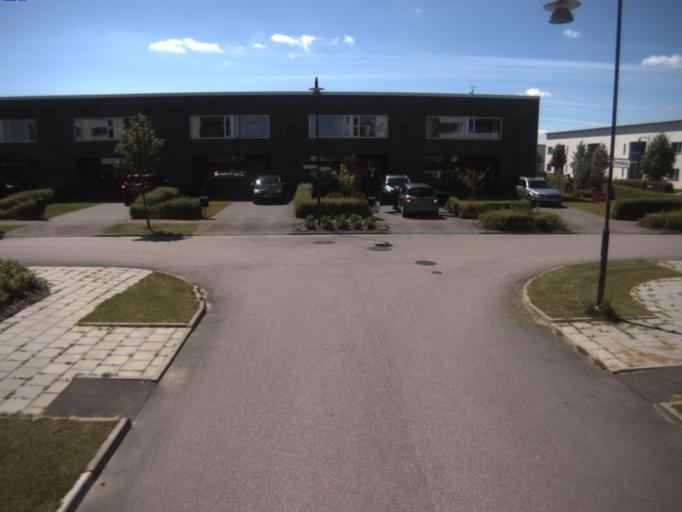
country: SE
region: Skane
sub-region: Helsingborg
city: Helsingborg
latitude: 56.0776
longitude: 12.7001
